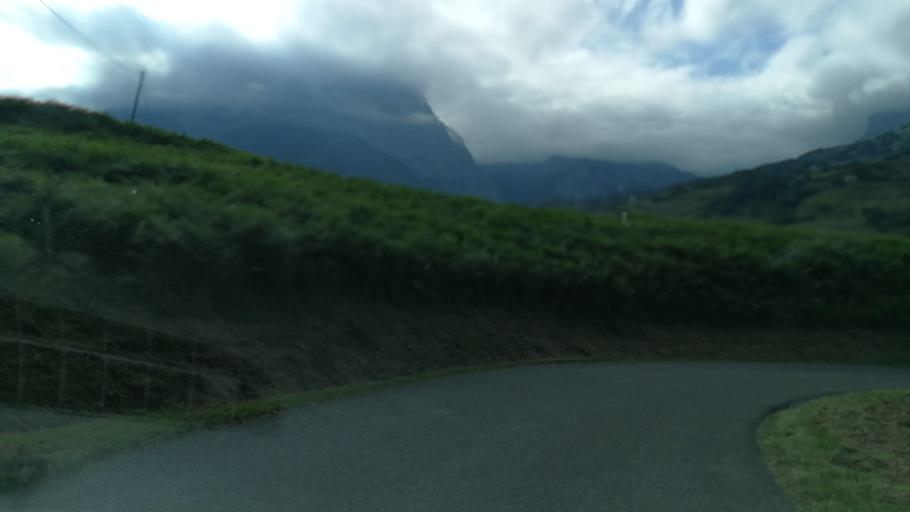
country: FR
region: Aquitaine
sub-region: Departement des Pyrenees-Atlantiques
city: Arette
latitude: 42.9257
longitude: -0.6408
